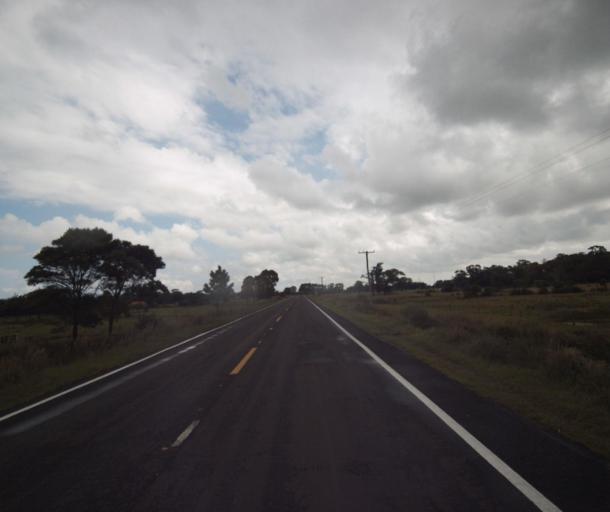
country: BR
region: Rio Grande do Sul
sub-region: Tapes
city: Tapes
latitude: -31.3185
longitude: -51.1215
